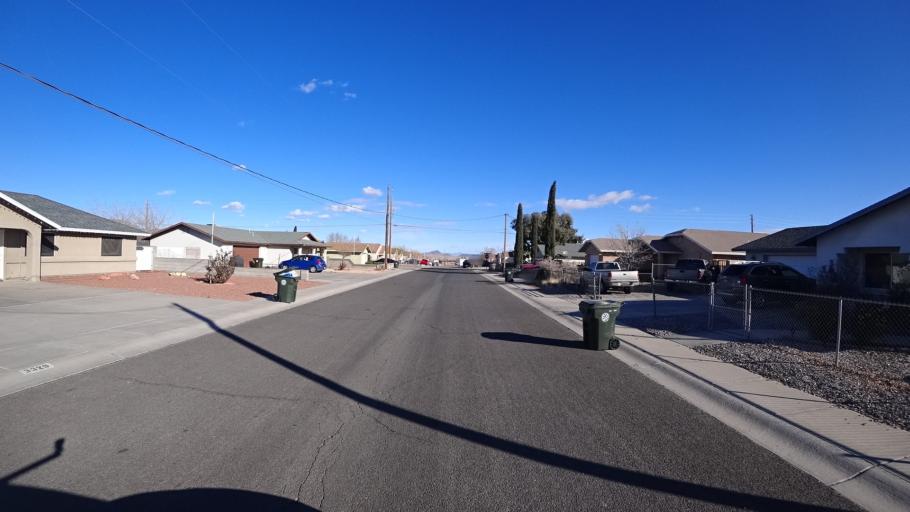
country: US
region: Arizona
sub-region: Mohave County
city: New Kingman-Butler
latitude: 35.2204
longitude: -113.9968
